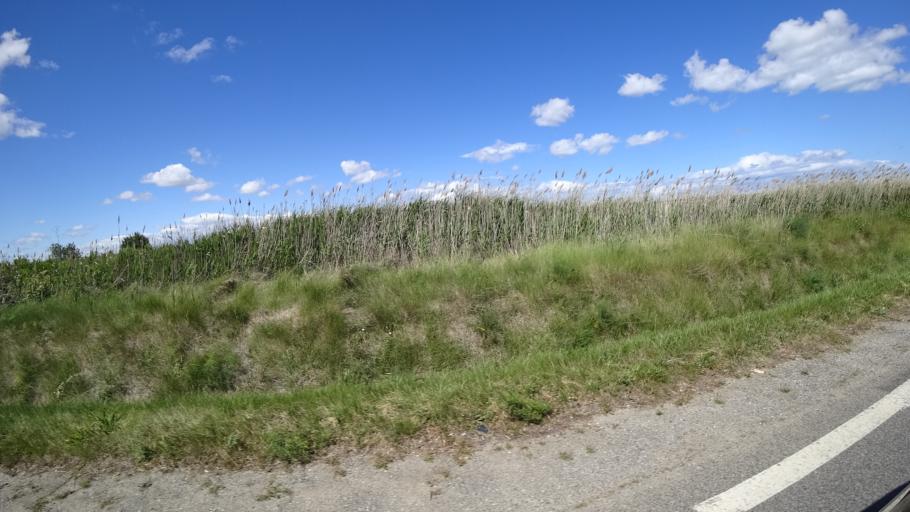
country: FR
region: Languedoc-Roussillon
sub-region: Departement des Pyrenees-Orientales
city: Saleilles
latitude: 42.6667
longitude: 2.9652
